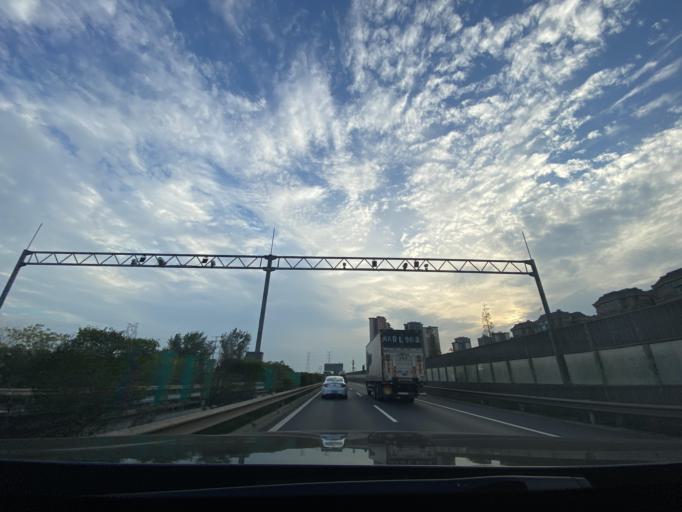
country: CN
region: Sichuan
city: Deyang
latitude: 31.0817
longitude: 104.3885
